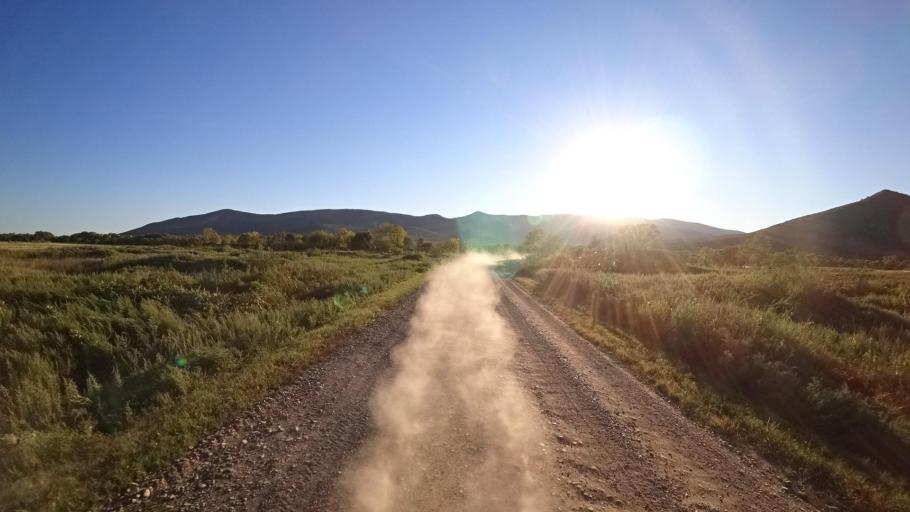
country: RU
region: Primorskiy
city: Kirovskiy
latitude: 44.8321
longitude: 133.5865
